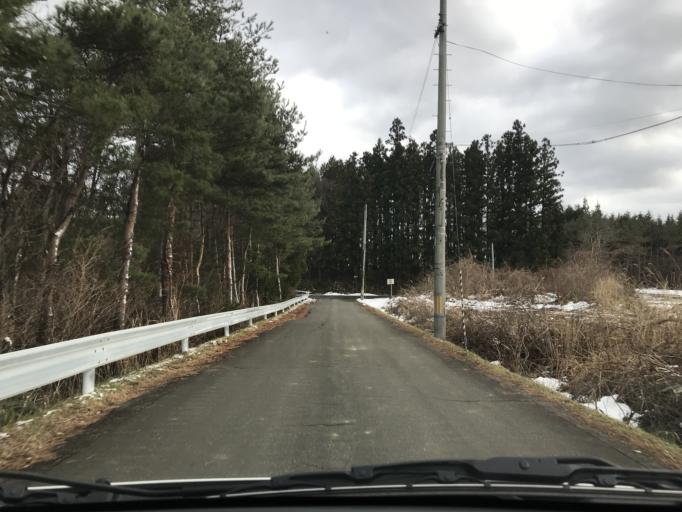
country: JP
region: Iwate
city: Ichinoseki
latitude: 38.9862
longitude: 141.0052
